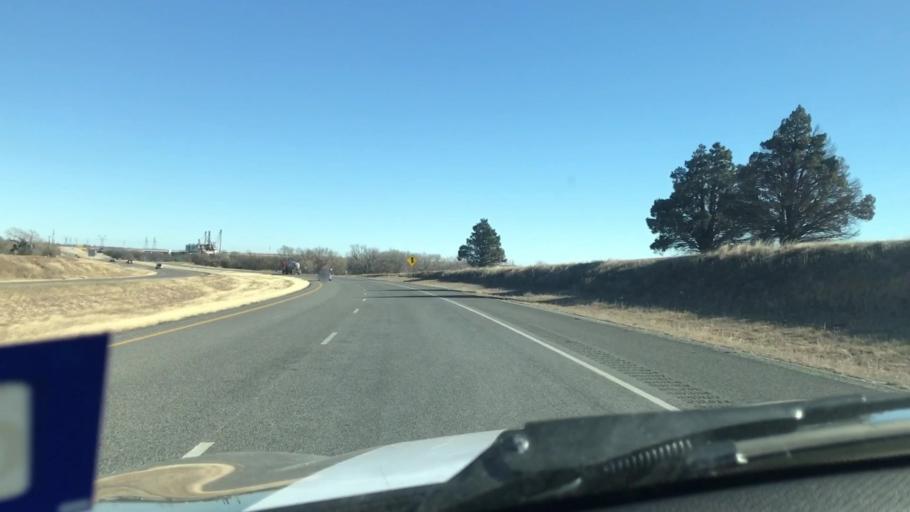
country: US
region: Texas
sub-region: Scurry County
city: Snyder
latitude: 32.6895
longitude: -100.8572
